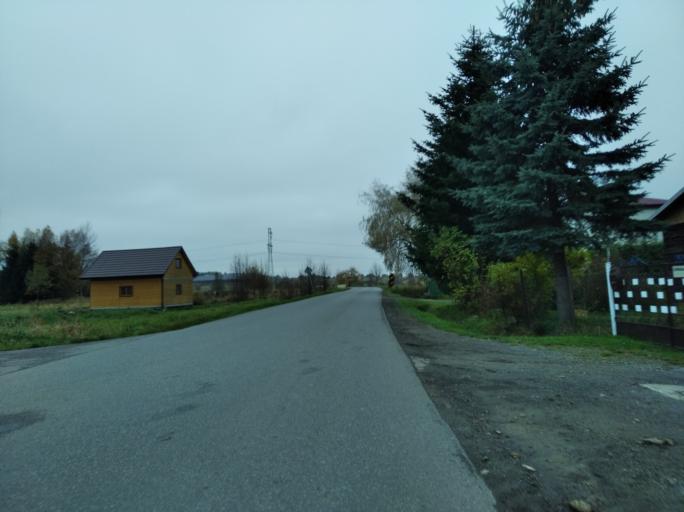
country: PL
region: Subcarpathian Voivodeship
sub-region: Powiat krosnienski
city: Odrzykon
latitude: 49.7222
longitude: 21.7626
